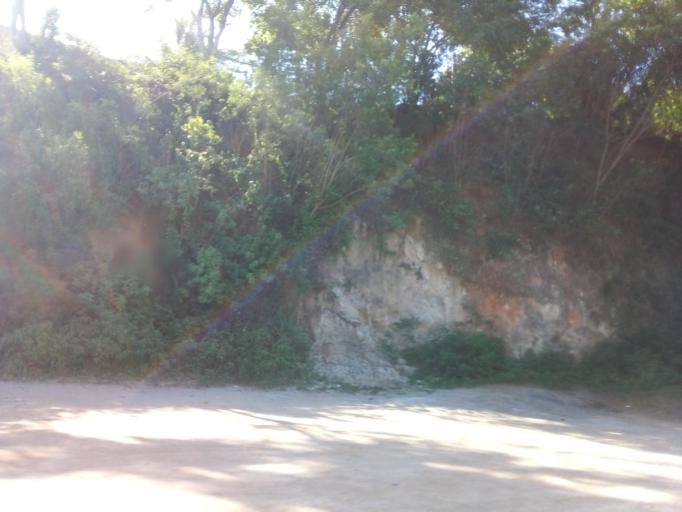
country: BR
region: Espirito Santo
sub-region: Vitoria
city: Vitoria
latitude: -20.2815
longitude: -40.3766
